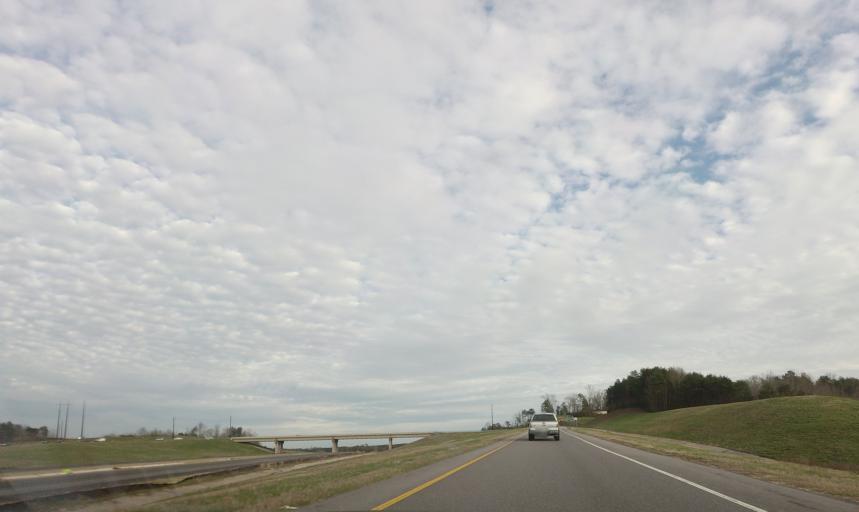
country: US
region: Alabama
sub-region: Jefferson County
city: Forestdale
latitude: 33.5886
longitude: -86.8592
